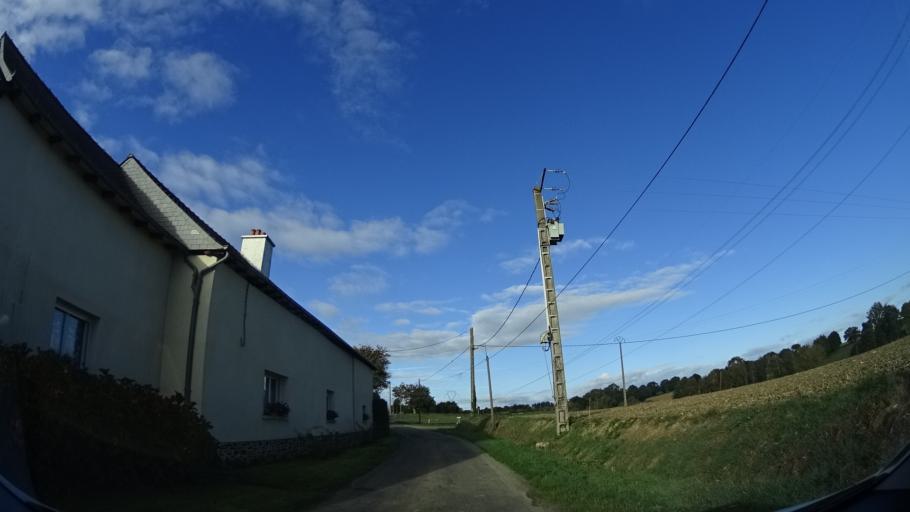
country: FR
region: Brittany
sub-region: Departement d'Ille-et-Vilaine
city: Geveze
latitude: 48.2016
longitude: -1.8161
